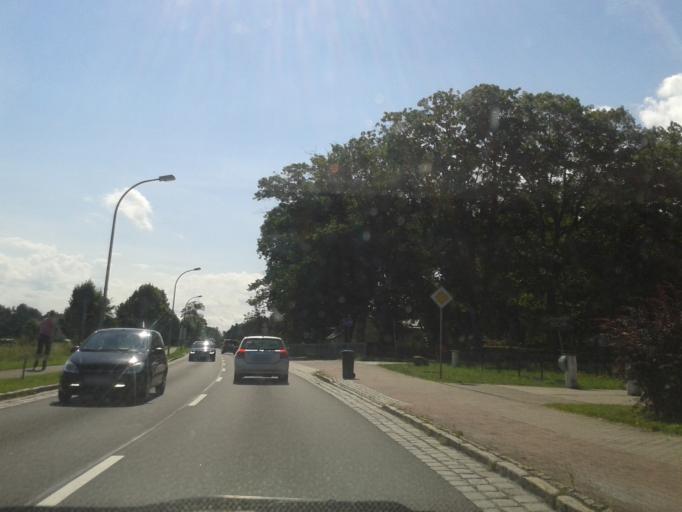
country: DE
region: Mecklenburg-Vorpommern
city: Jatznick
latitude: 53.5723
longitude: 13.9482
